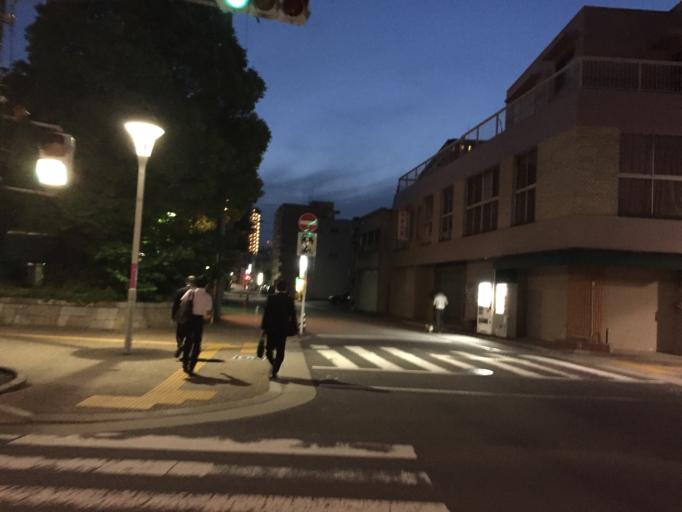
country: JP
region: Mie
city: Yokkaichi
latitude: 34.9656
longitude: 136.6257
